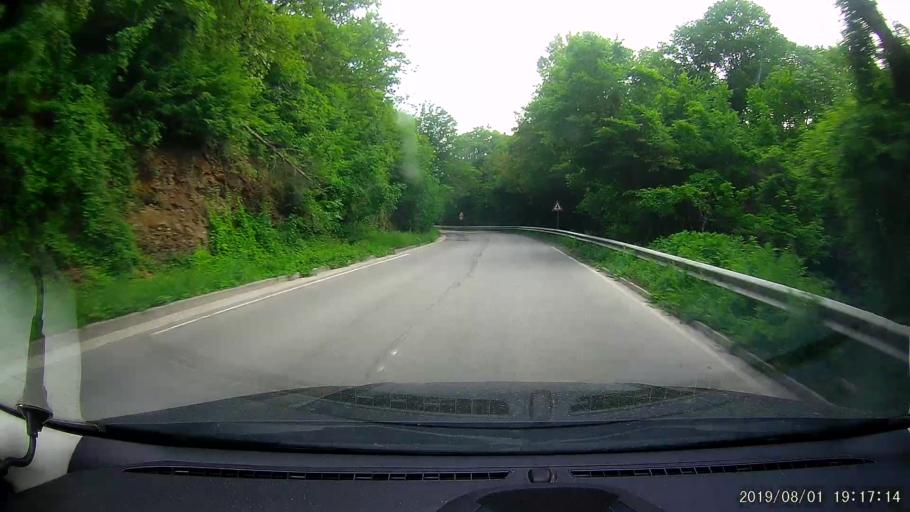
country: BG
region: Shumen
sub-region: Obshtina Smyadovo
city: Smyadovo
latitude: 42.9255
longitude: 26.9442
